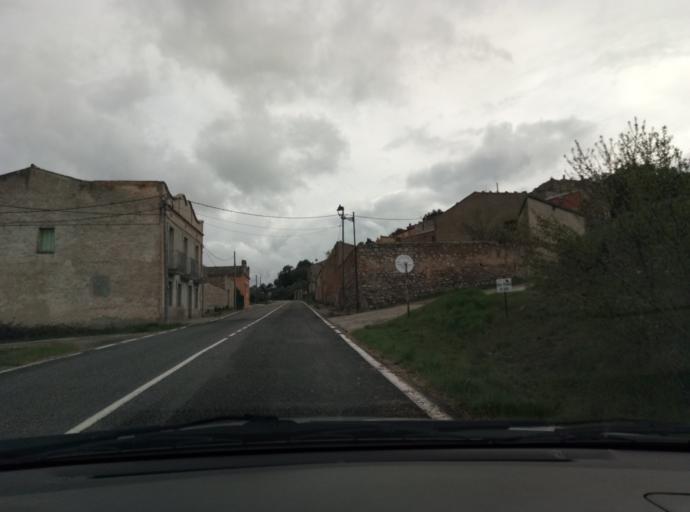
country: ES
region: Catalonia
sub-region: Provincia de Tarragona
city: Santa Coloma de Queralt
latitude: 41.5992
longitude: 1.3479
